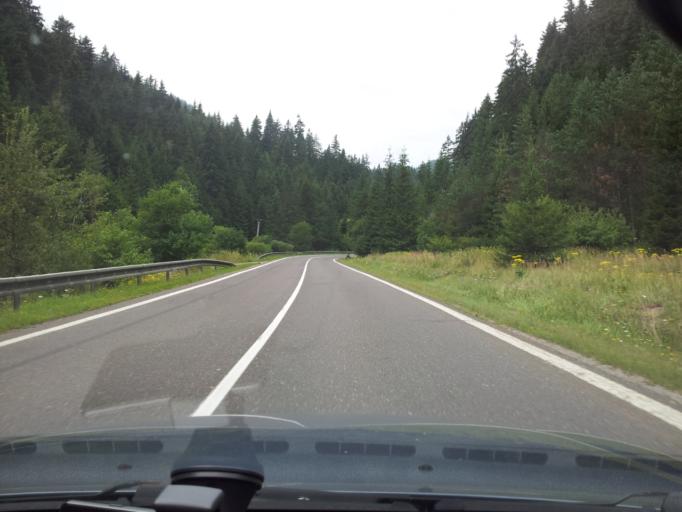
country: SK
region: Zilinsky
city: Ruzomberok
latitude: 49.1265
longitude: 19.2916
